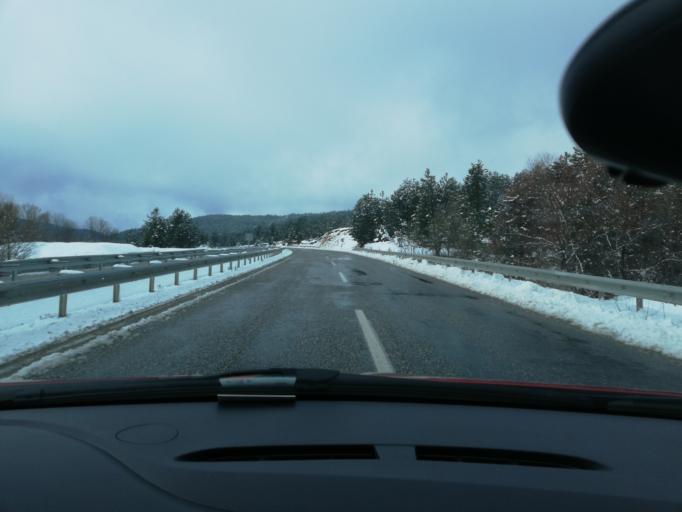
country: TR
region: Kastamonu
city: Akkaya
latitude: 41.2871
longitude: 33.4419
